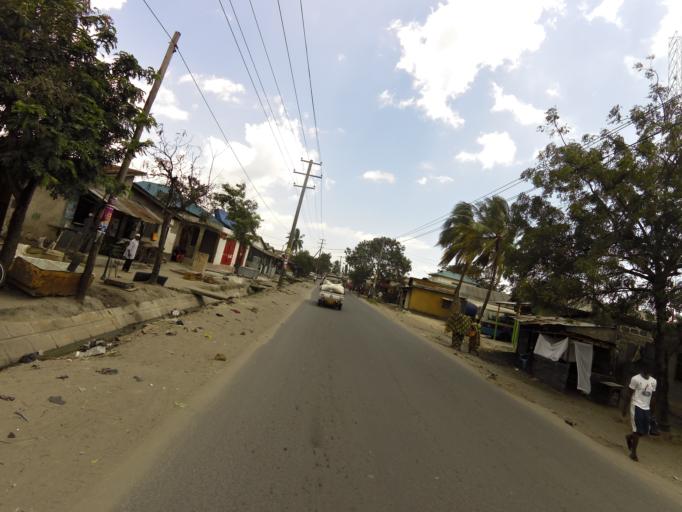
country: TZ
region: Dar es Salaam
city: Magomeni
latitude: -6.7936
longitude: 39.2463
